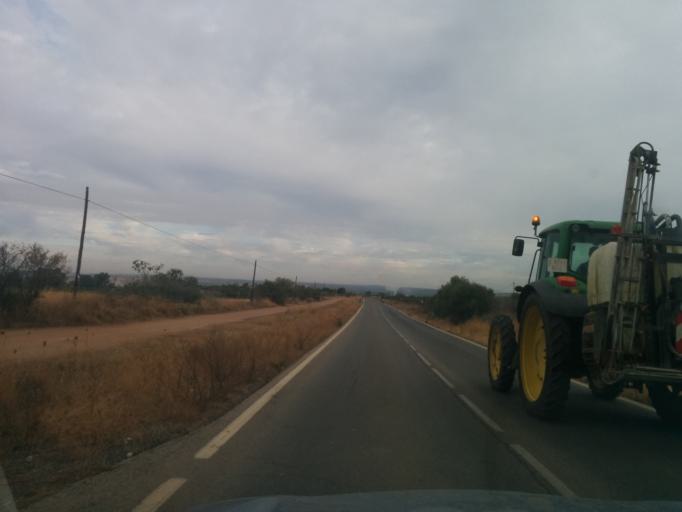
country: ES
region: Andalusia
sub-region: Provincia de Sevilla
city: Guillena
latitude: 37.5194
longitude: -6.0296
